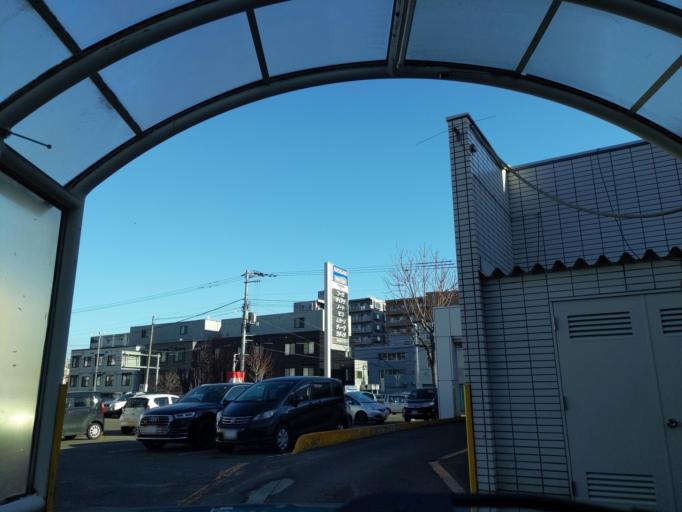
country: JP
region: Hokkaido
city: Sapporo
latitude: 43.0636
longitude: 141.3250
